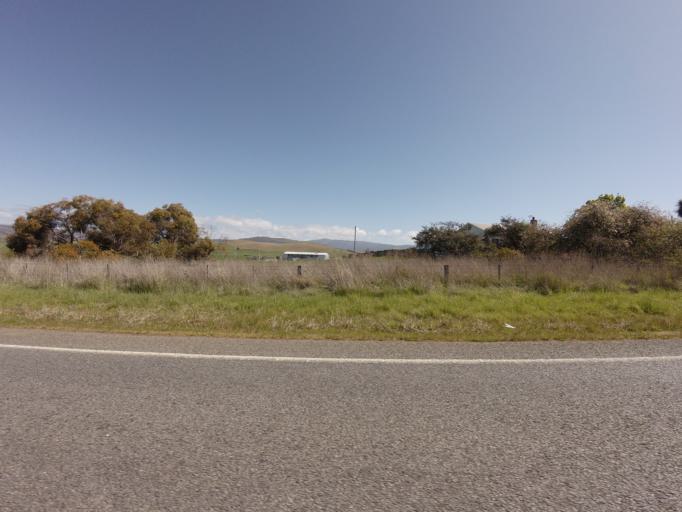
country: AU
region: Tasmania
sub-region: Derwent Valley
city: New Norfolk
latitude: -42.5545
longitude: 146.8048
